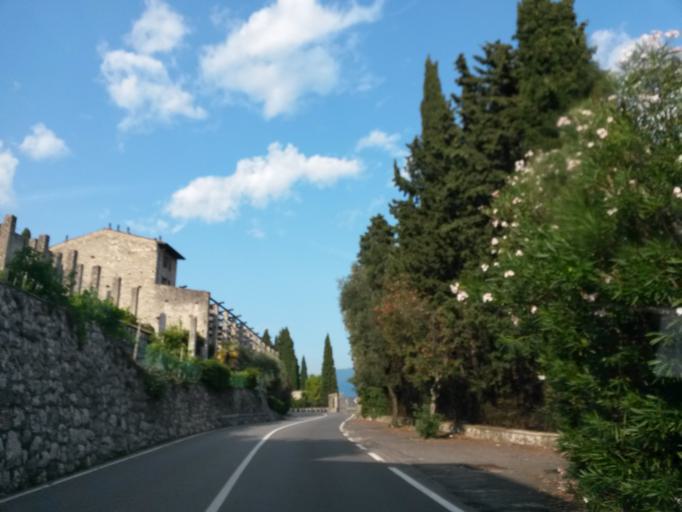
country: IT
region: Lombardy
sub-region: Provincia di Brescia
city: Gargnano
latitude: 45.6957
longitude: 10.6702
